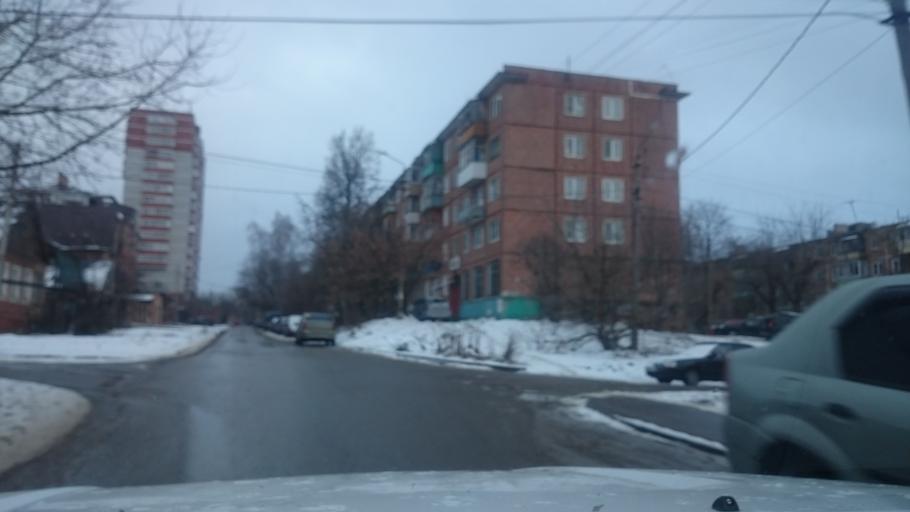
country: RU
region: Tula
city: Mendeleyevskiy
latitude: 54.1794
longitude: 37.5698
